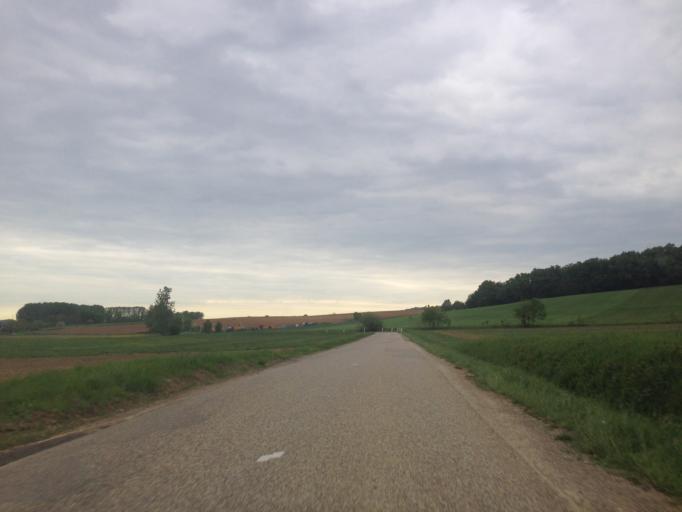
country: FR
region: Alsace
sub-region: Departement du Bas-Rhin
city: Hochfelden
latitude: 48.7766
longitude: 7.5731
